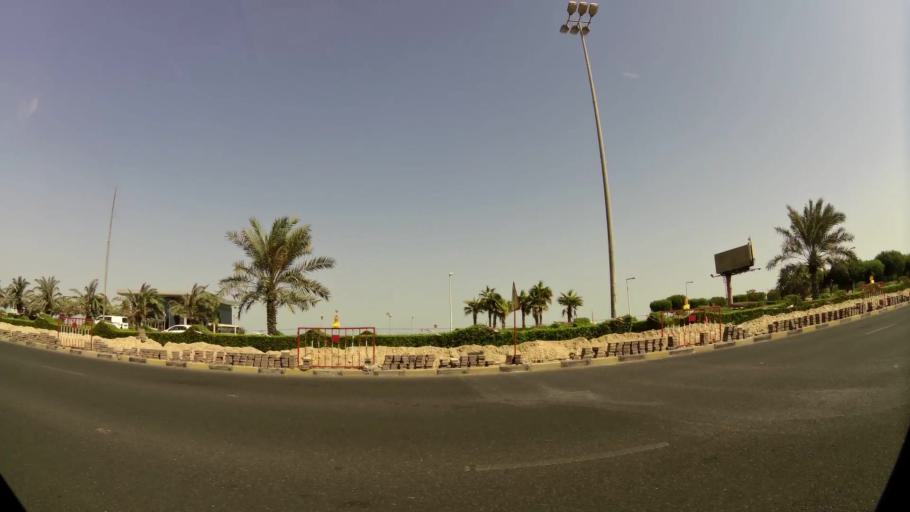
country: KW
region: Al Asimah
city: Ad Dasmah
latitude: 29.3660
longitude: 48.0213
